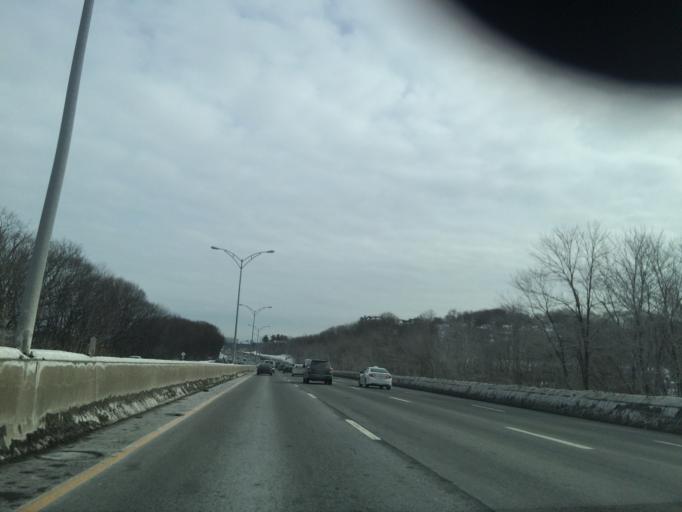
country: US
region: Massachusetts
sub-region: Middlesex County
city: Watertown
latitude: 42.3576
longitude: -71.1718
